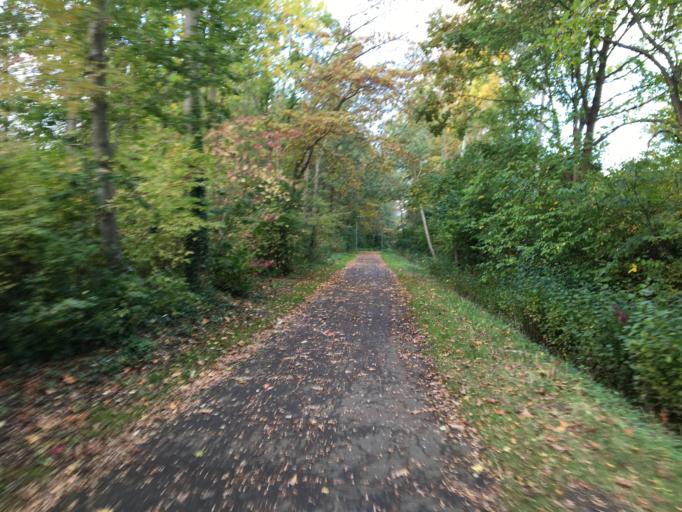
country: DE
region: Lower Saxony
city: Braunschweig
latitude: 52.2812
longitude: 10.5161
